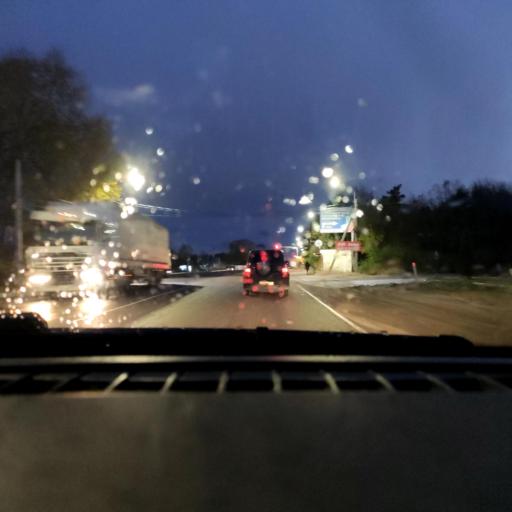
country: RU
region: Voronezj
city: Maslovka
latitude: 51.6360
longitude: 39.2909
